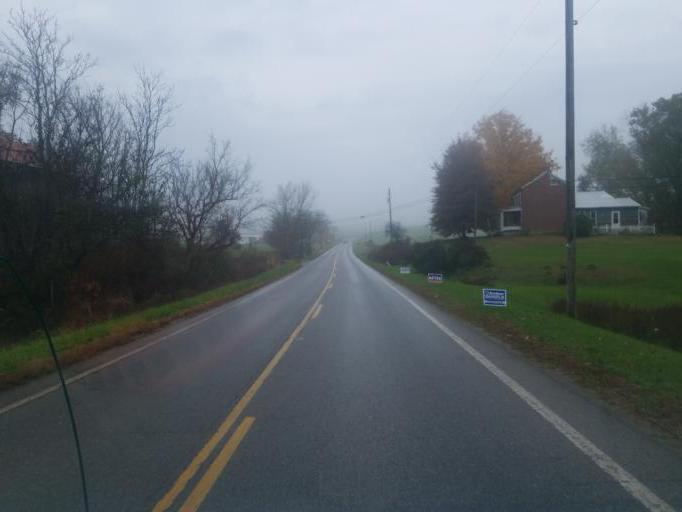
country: US
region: Ohio
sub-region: Morgan County
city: McConnelsville
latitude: 39.5031
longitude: -81.8557
